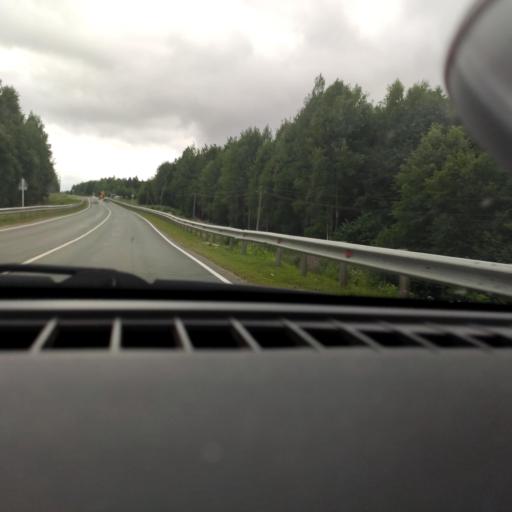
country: RU
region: Perm
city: Polazna
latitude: 58.3123
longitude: 56.1509
